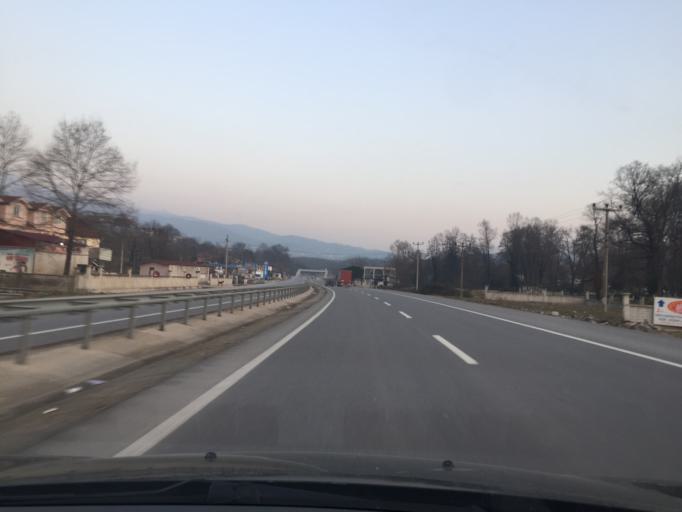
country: TR
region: Sakarya
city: Akyazi
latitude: 40.6321
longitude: 30.6335
